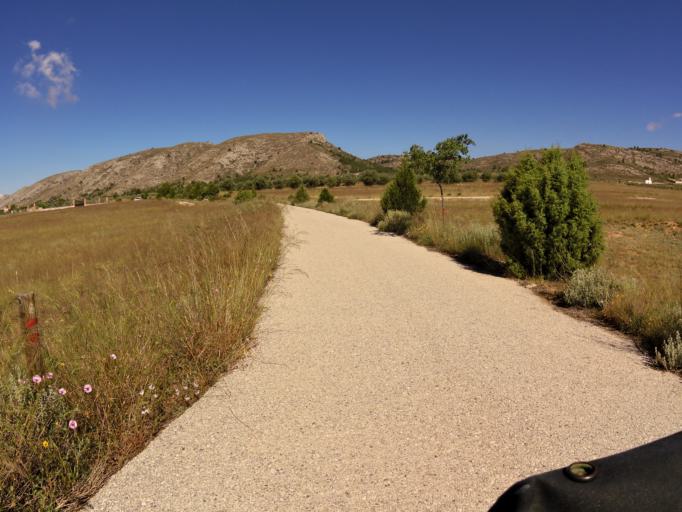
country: ES
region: Valencia
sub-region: Provincia de Alicante
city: Canada
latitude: 38.6431
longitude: -0.8125
